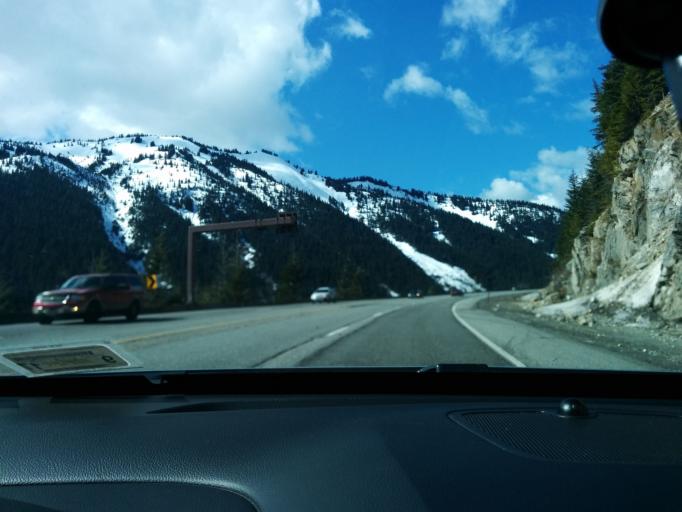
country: US
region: Washington
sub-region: Chelan County
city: Leavenworth
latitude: 47.7224
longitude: -121.1377
